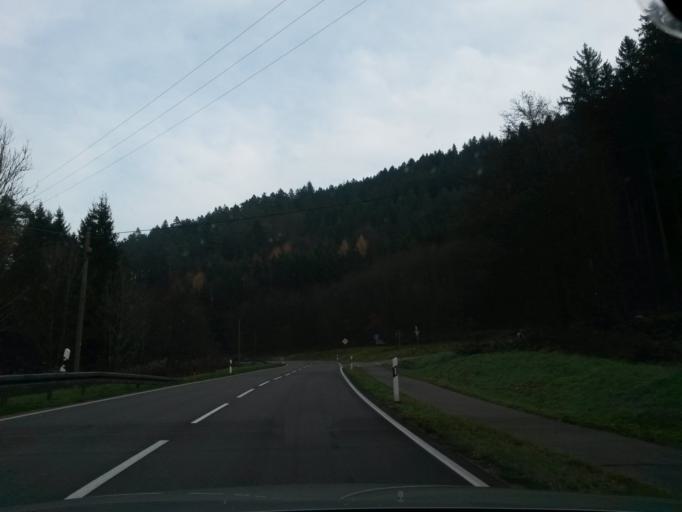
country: DE
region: Baden-Wuerttemberg
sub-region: Freiburg Region
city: Schenkenzell
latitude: 48.3172
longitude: 8.3874
